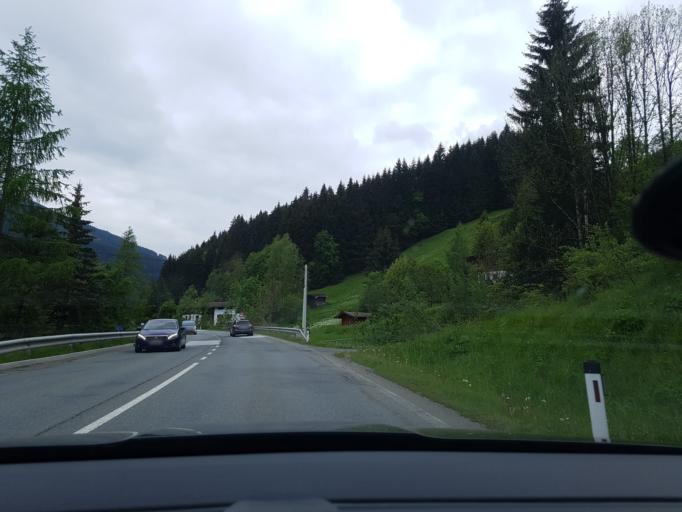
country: AT
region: Tyrol
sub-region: Politischer Bezirk Kitzbuhel
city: Jochberg
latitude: 47.3574
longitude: 12.4136
